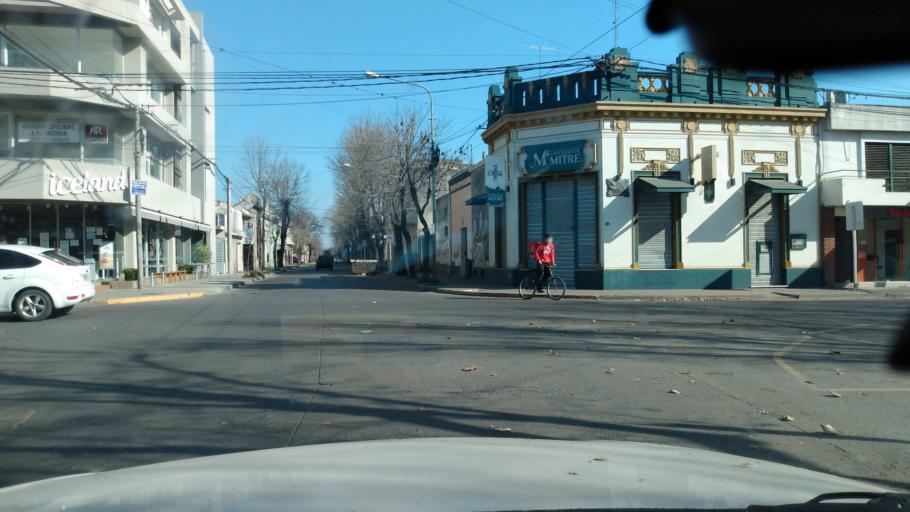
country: AR
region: Buenos Aires
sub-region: Partido de Lujan
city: Lujan
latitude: -34.5670
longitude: -59.1143
